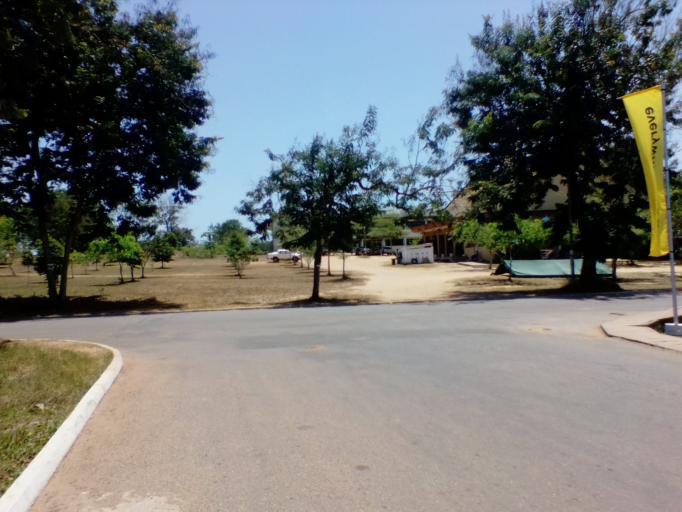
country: GH
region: Central
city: Cape Coast
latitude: 5.1202
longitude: -1.2916
